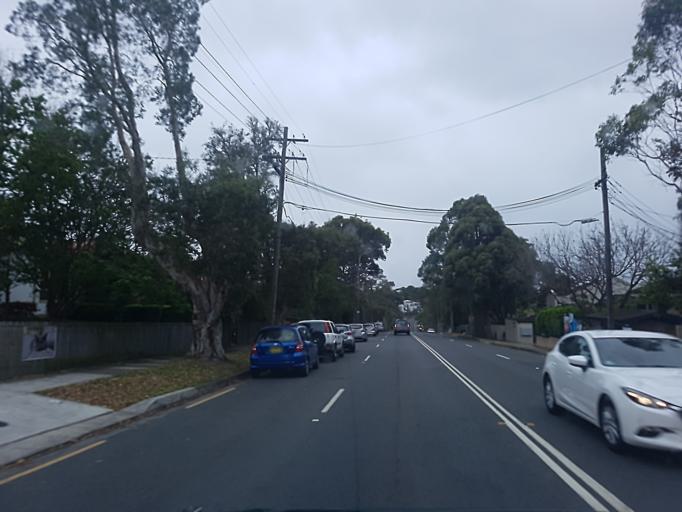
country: AU
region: New South Wales
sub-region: North Sydney
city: Cammeray
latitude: -33.8087
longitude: 151.2082
